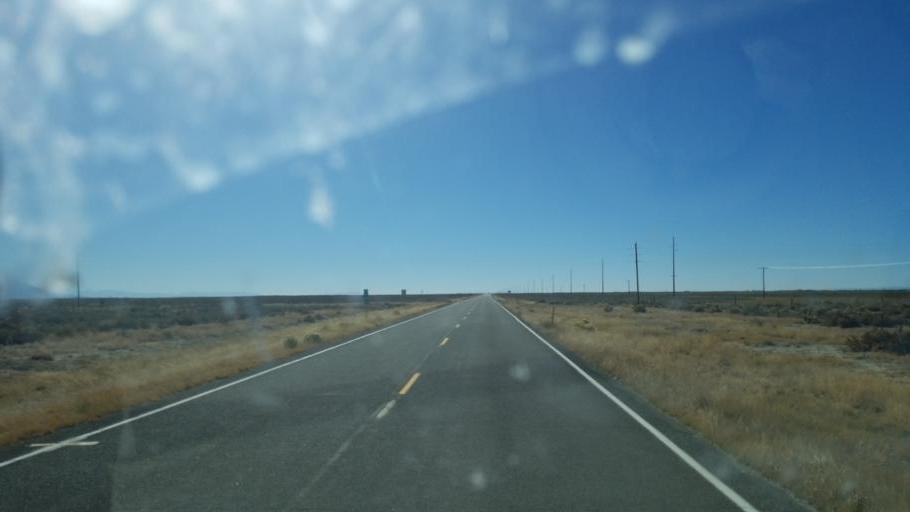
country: US
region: Colorado
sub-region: Saguache County
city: Center
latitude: 37.9206
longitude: -105.8997
